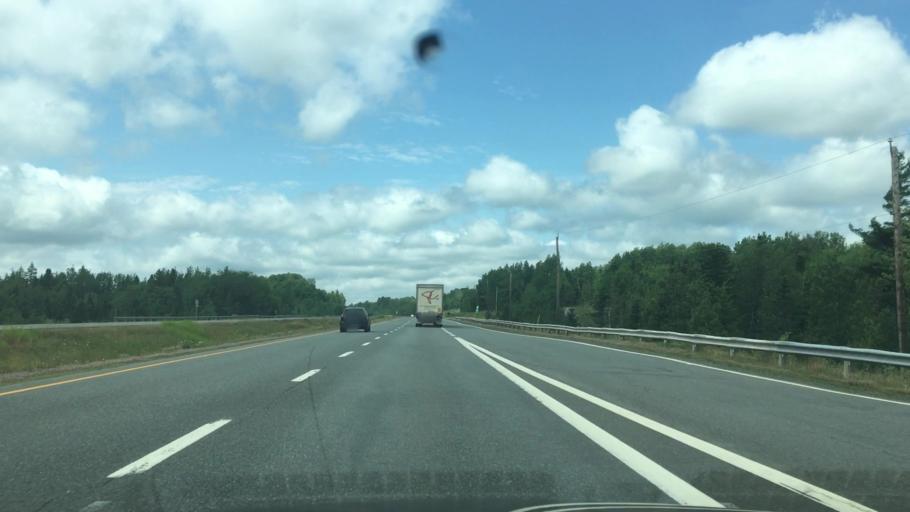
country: CA
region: Nova Scotia
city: Oxford
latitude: 45.7229
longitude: -63.8858
